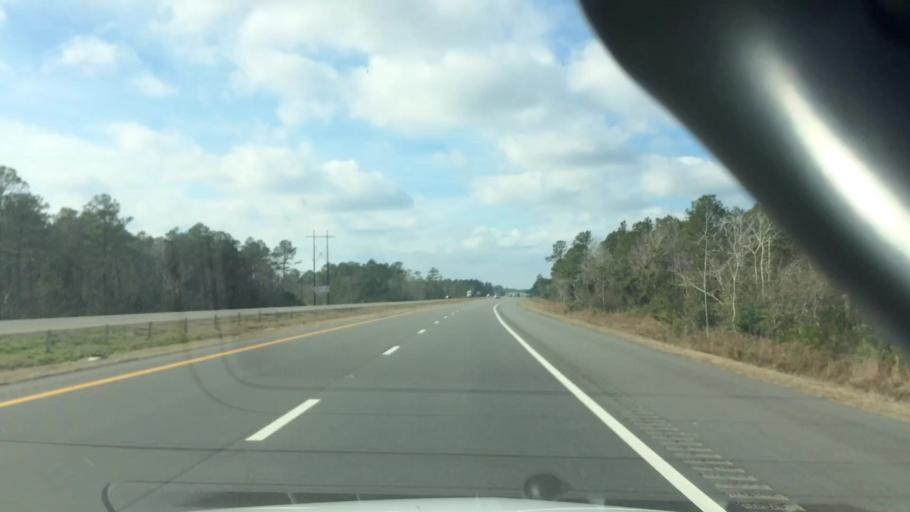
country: US
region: North Carolina
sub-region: Brunswick County
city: Leland
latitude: 34.2739
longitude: -78.0331
